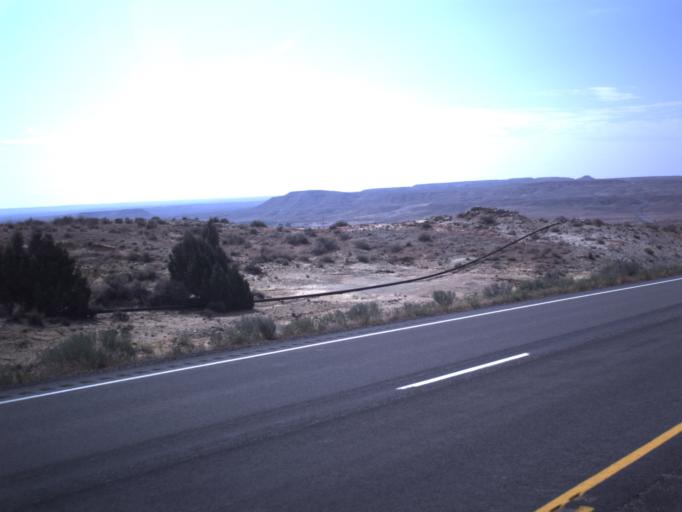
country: US
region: Utah
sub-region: Uintah County
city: Naples
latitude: 40.3294
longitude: -109.4863
